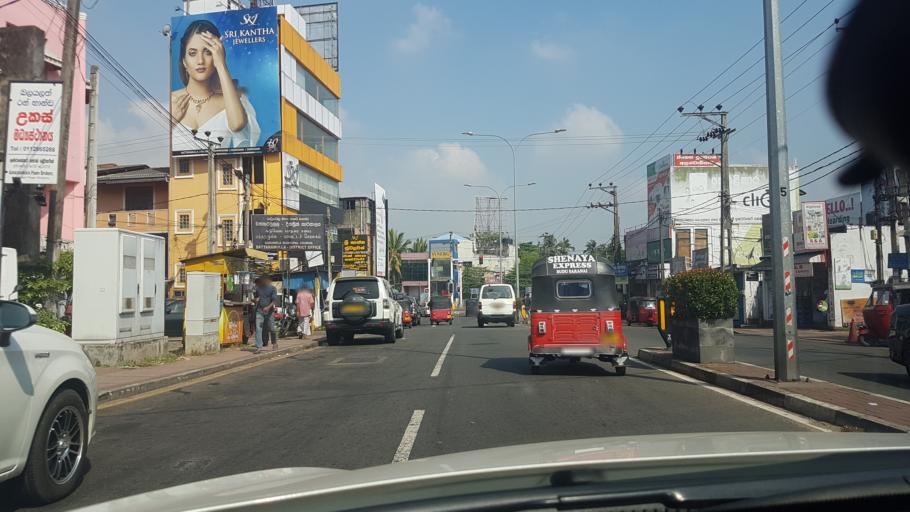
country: LK
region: Western
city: Battaramulla South
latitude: 6.9013
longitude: 79.9198
